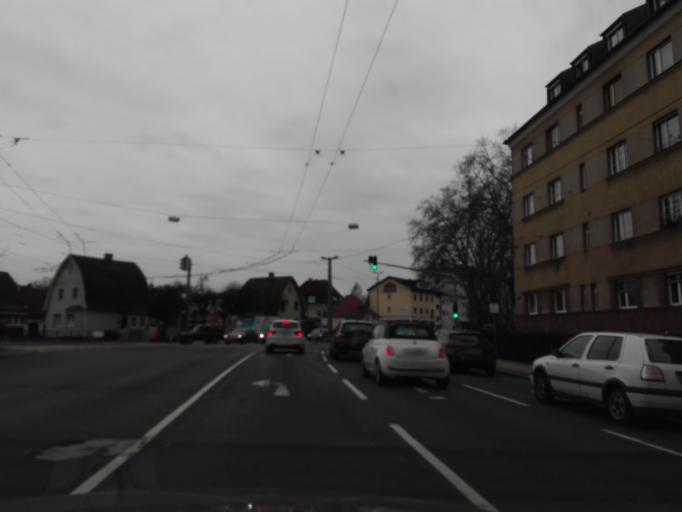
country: AT
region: Upper Austria
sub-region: Linz Stadt
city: Linz
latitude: 48.2842
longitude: 14.2922
